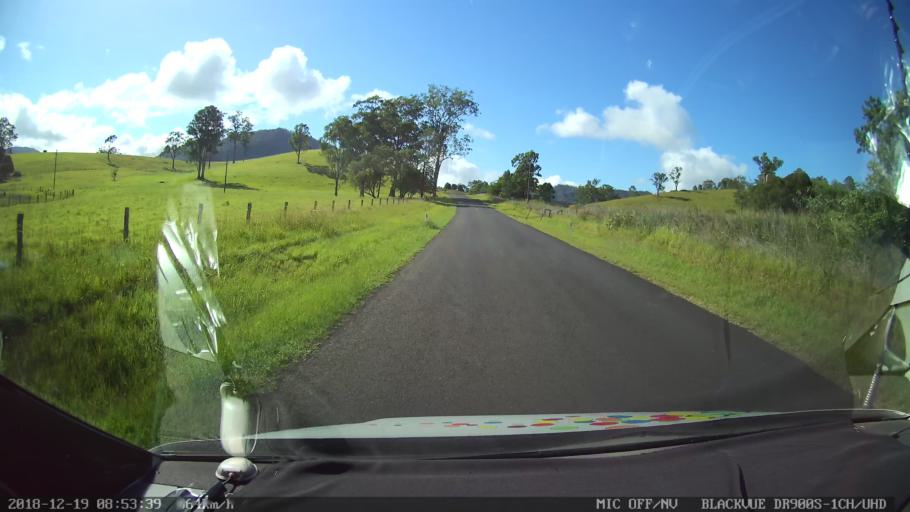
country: AU
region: New South Wales
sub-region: Kyogle
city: Kyogle
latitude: -28.4036
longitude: 152.9785
